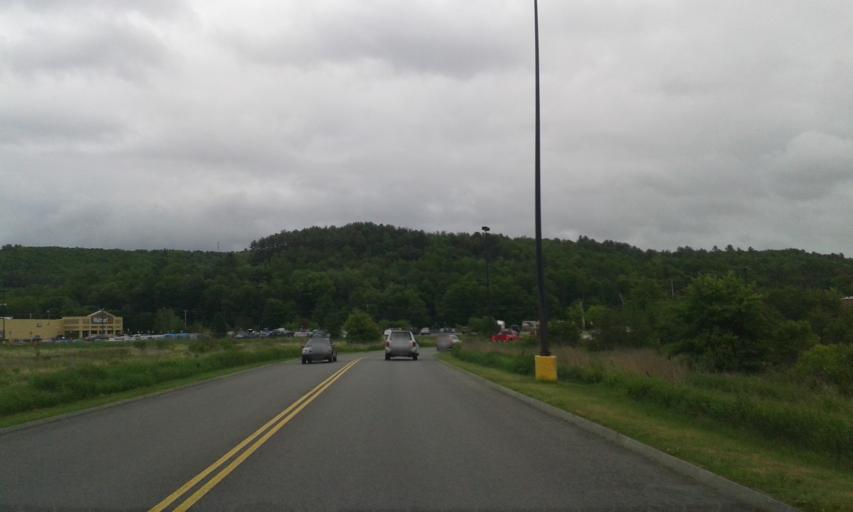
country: US
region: New Hampshire
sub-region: Grafton County
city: Littleton
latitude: 44.3051
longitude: -71.8023
